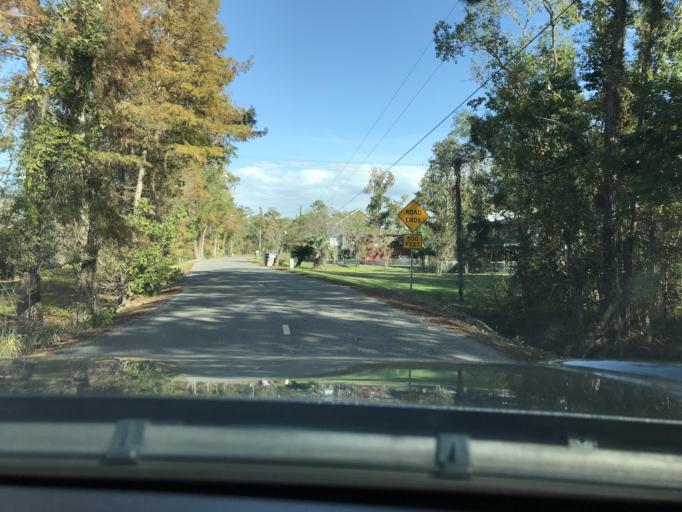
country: US
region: Louisiana
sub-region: Calcasieu Parish
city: Westlake
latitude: 30.3148
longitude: -93.2858
